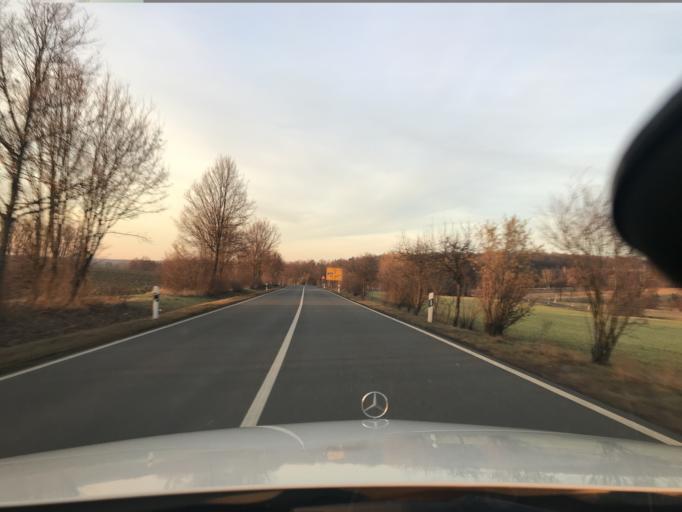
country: DE
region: Thuringia
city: Ernstroda
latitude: 50.8752
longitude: 10.6581
